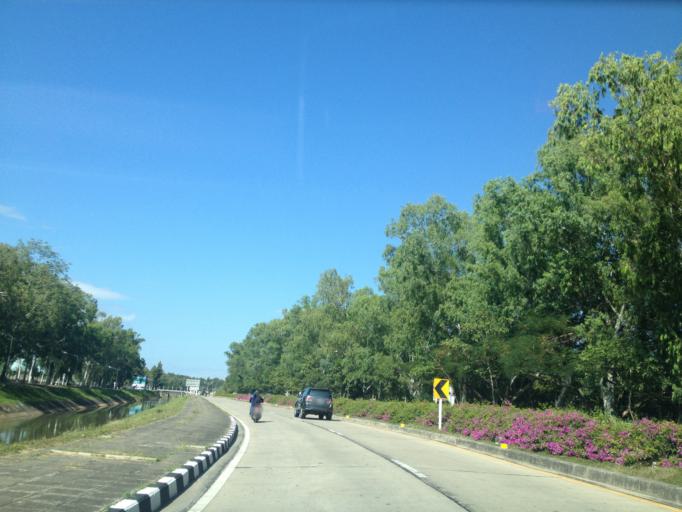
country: TH
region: Chiang Mai
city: Chiang Mai
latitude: 18.8565
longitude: 98.9623
